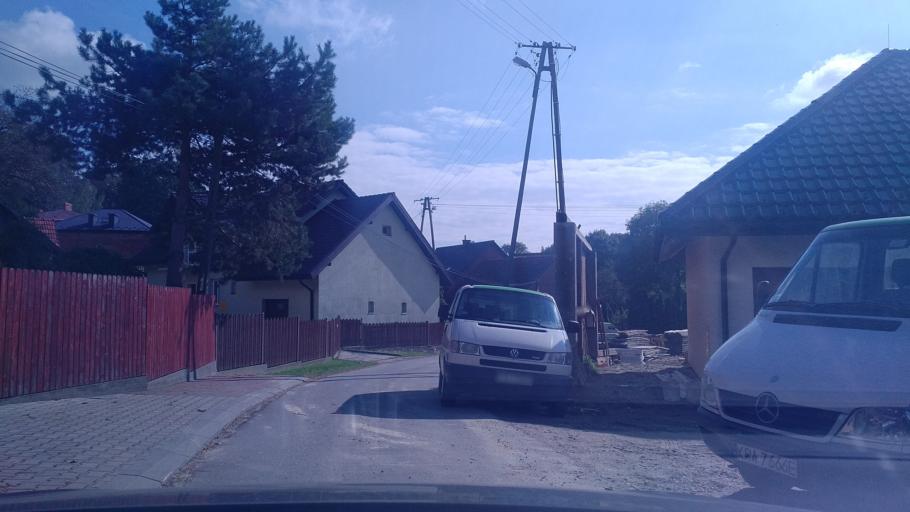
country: PL
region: Lesser Poland Voivodeship
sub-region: Powiat krakowski
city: Wielka Wies
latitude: 50.1355
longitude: 19.8382
